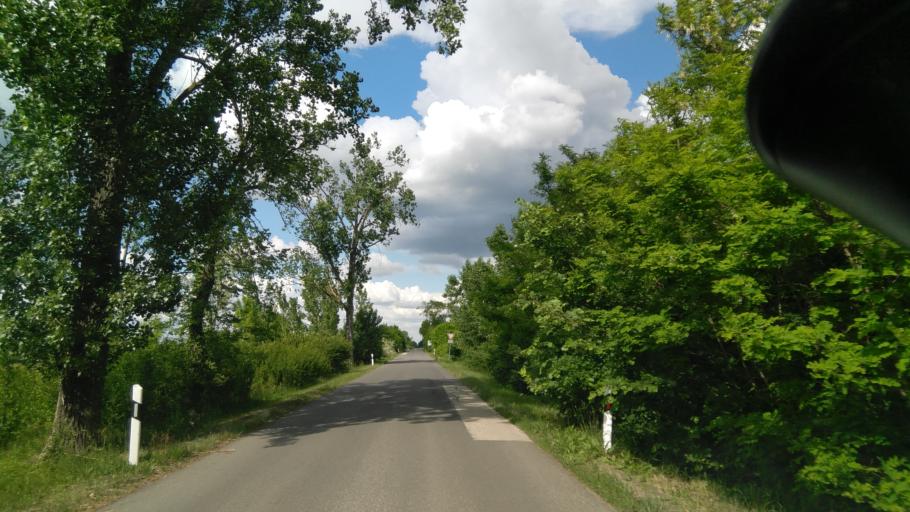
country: HU
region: Bekes
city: Bucsa
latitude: 47.1626
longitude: 21.0865
